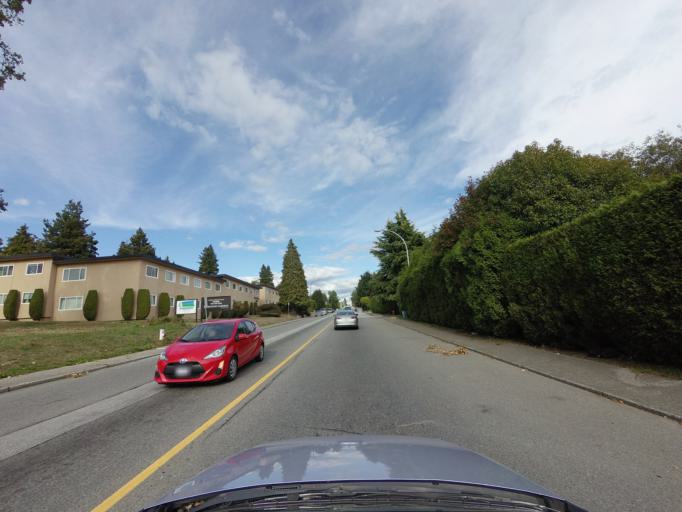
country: CA
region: British Columbia
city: New Westminster
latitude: 49.2250
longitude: -122.9163
